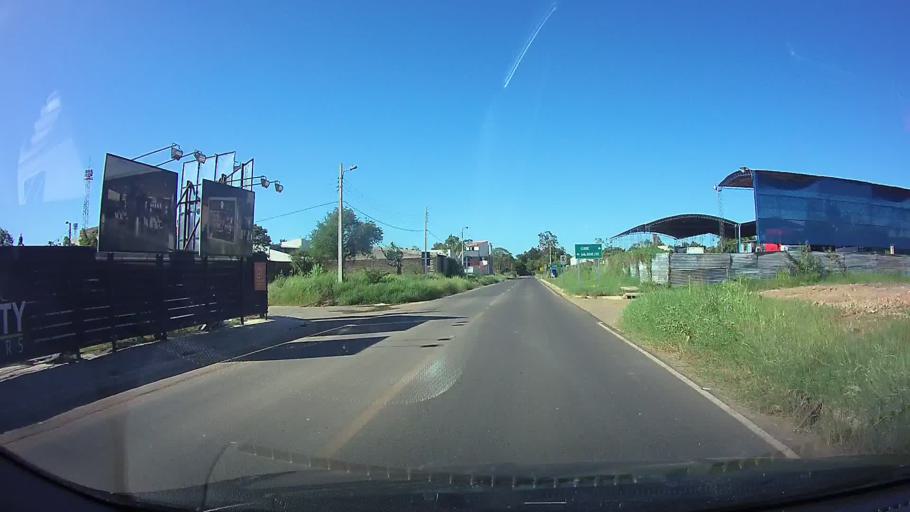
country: PY
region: Central
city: Fernando de la Mora
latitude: -25.2884
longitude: -57.5422
